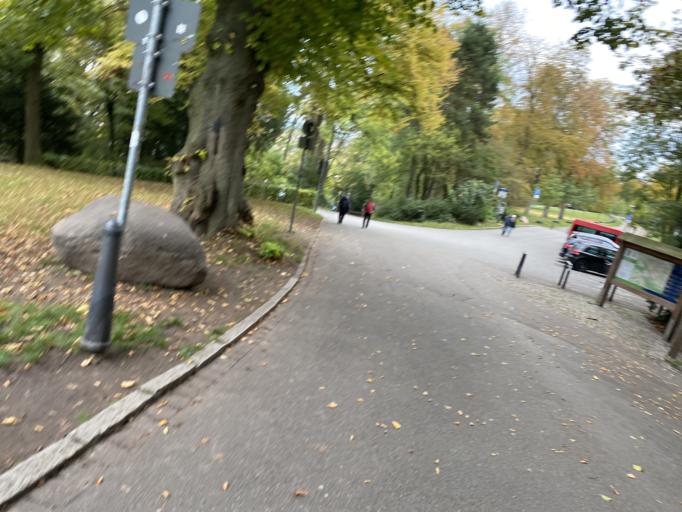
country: DE
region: North Rhine-Westphalia
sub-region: Regierungsbezirk Detmold
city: Bielefeld
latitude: 52.0143
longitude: 8.5284
